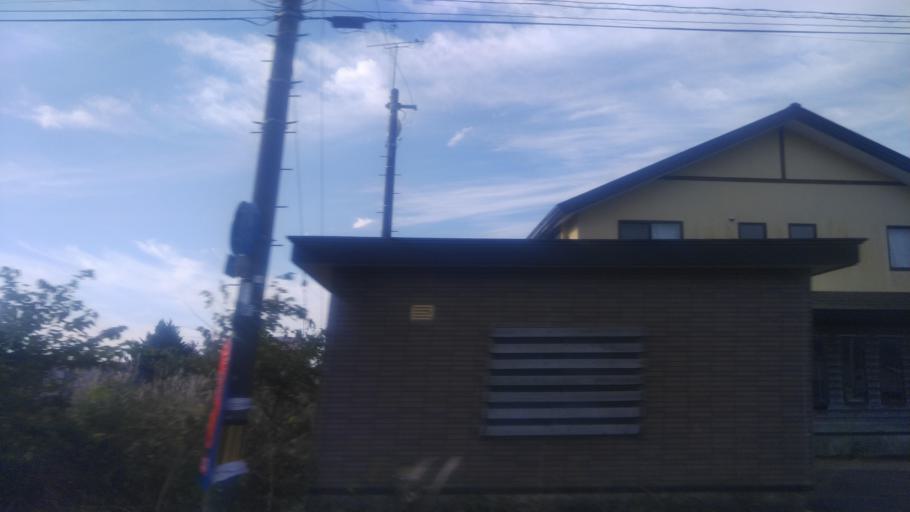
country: JP
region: Akita
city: Takanosu
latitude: 40.2519
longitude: 140.3798
